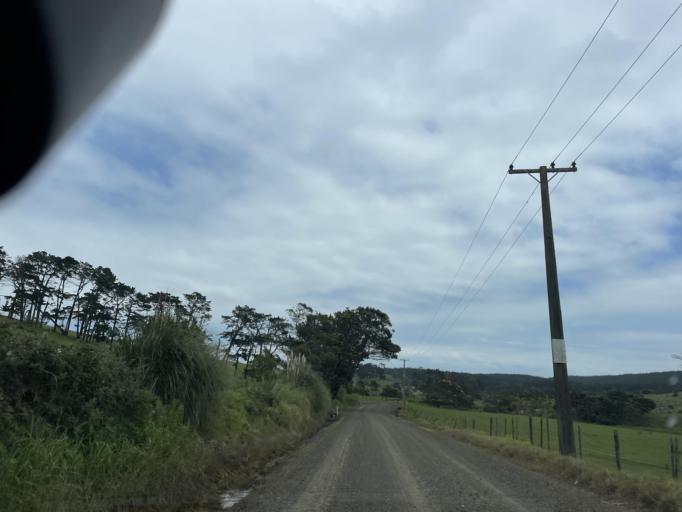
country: NZ
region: Auckland
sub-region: Auckland
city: Wellsford
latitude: -36.2546
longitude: 174.2379
